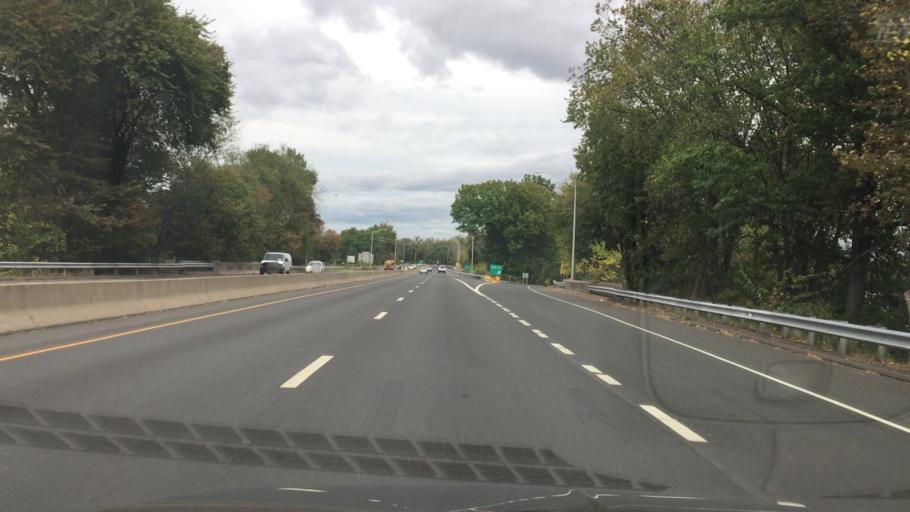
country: US
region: Connecticut
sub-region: Hartford County
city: Wethersfield
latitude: 41.7243
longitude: -72.6709
